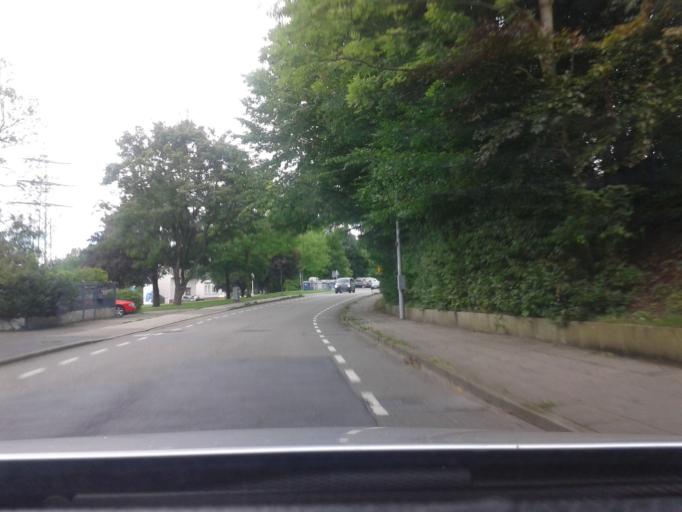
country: DE
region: North Rhine-Westphalia
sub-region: Regierungsbezirk Dusseldorf
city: Muelheim (Ruhr)
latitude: 51.4186
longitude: 6.8442
